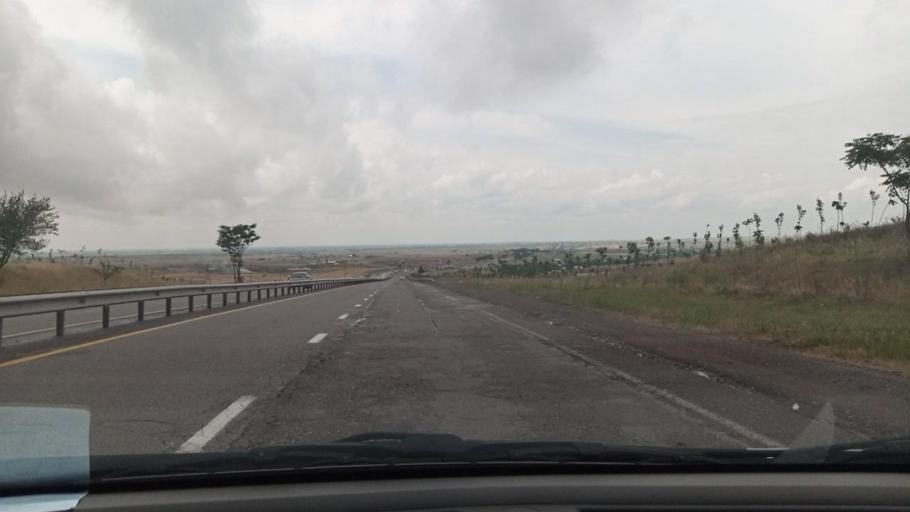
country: UZ
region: Toshkent
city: Ohangaron
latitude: 40.9644
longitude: 69.5541
